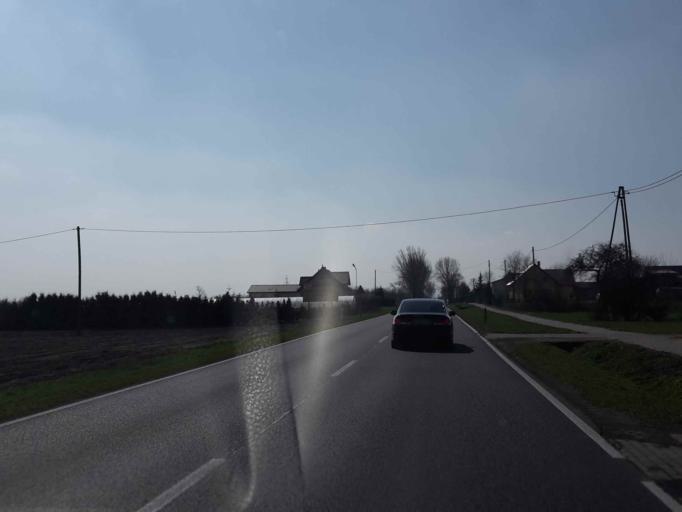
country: PL
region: Kujawsko-Pomorskie
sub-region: Powiat golubsko-dobrzynski
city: Kowalewo Pomorskie
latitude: 53.1486
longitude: 18.8823
